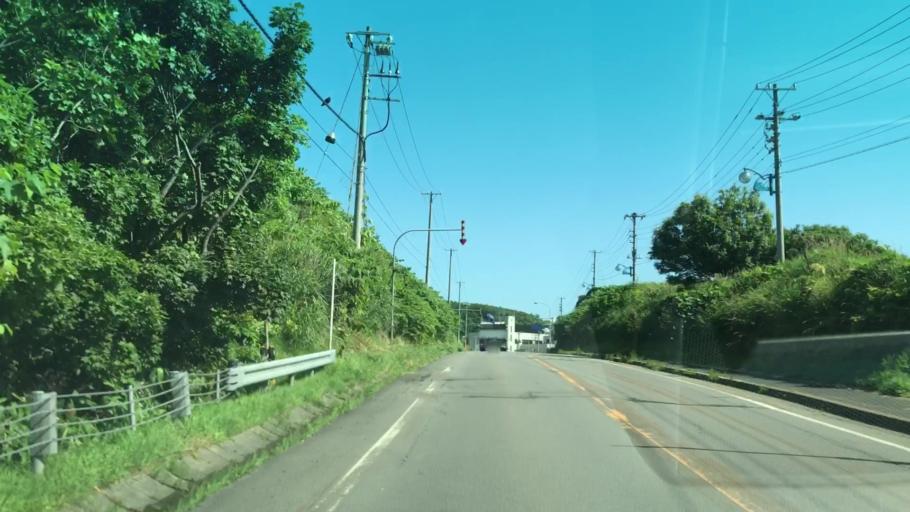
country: JP
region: Hokkaido
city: Iwanai
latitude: 43.0660
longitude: 140.4971
